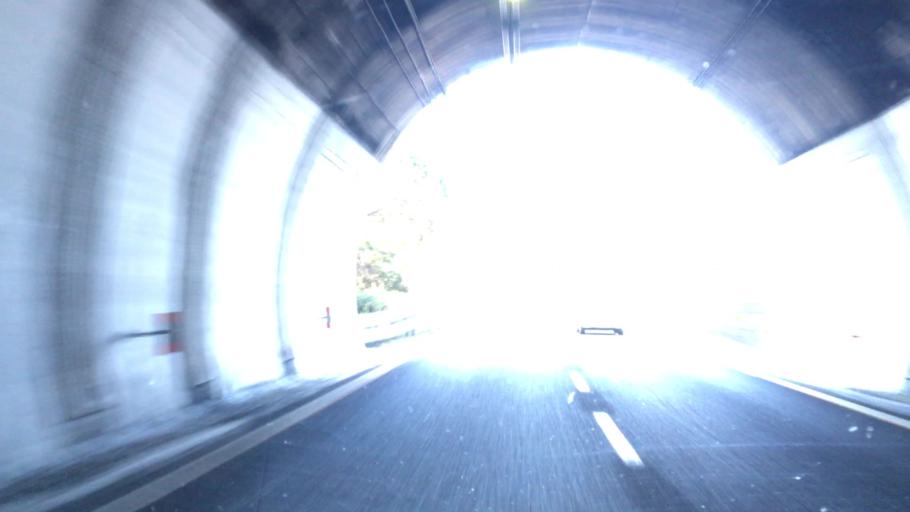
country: IT
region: Liguria
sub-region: Provincia di Genova
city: Chiavari
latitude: 44.3245
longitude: 9.3325
